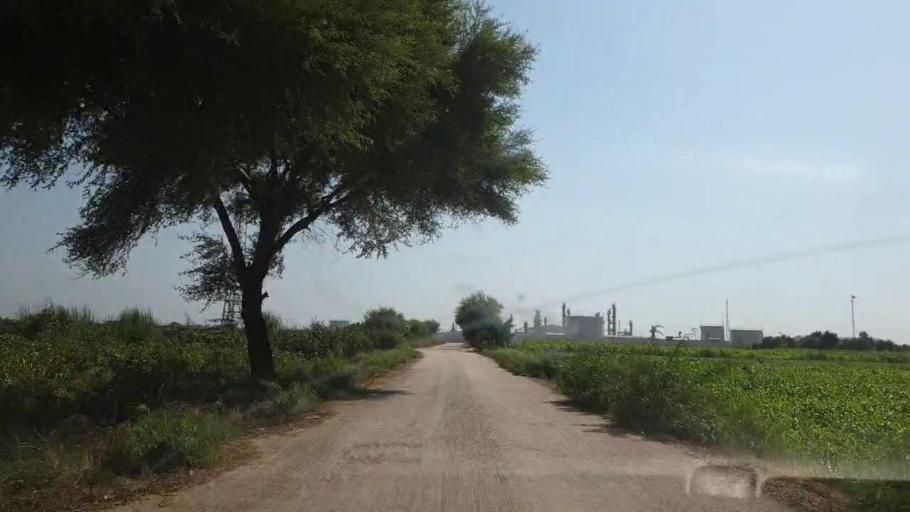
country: PK
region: Sindh
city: Tando Jam
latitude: 25.3911
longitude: 68.5820
